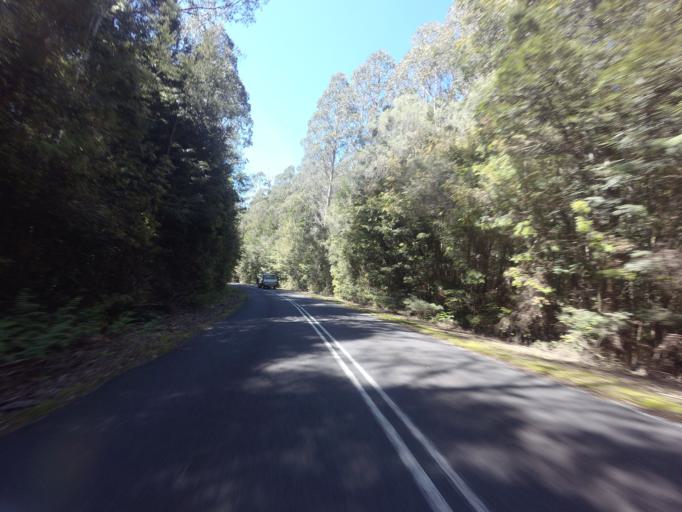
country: AU
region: Tasmania
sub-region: Huon Valley
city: Geeveston
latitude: -42.8234
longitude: 146.3323
